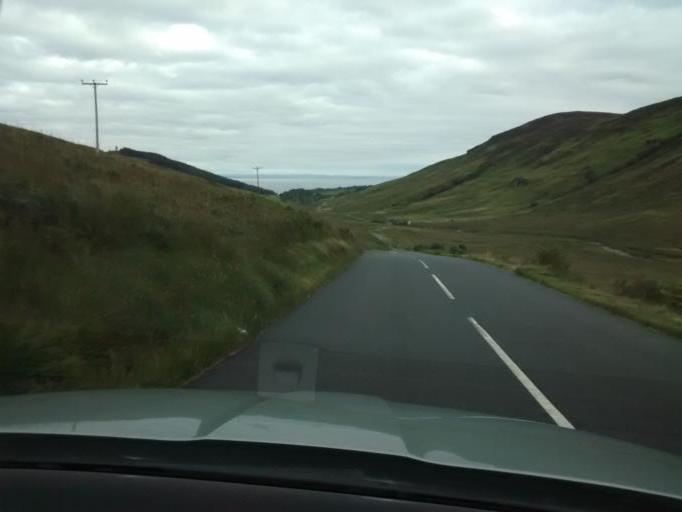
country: GB
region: Scotland
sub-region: North Ayrshire
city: Isle of Arran
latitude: 55.6758
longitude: -5.2047
